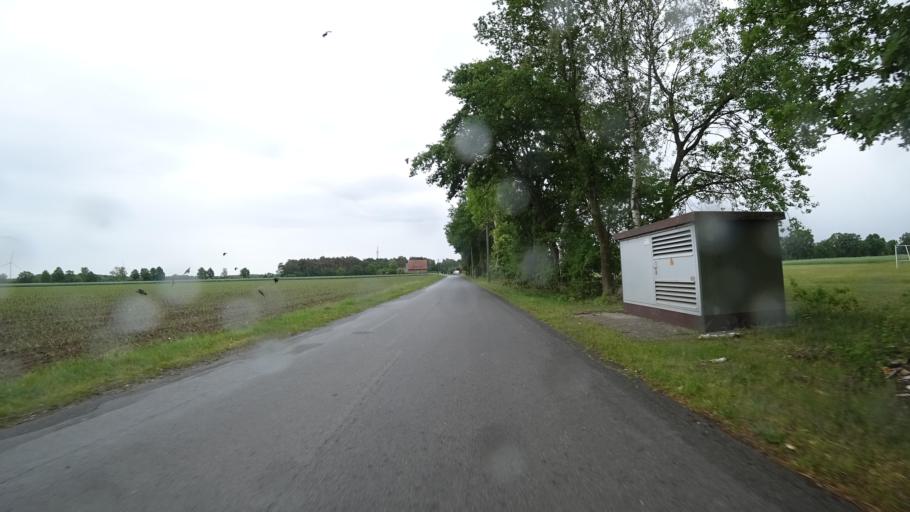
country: DE
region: North Rhine-Westphalia
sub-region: Regierungsbezirk Detmold
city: Rheda-Wiedenbruck
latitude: 51.9005
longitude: 8.3001
